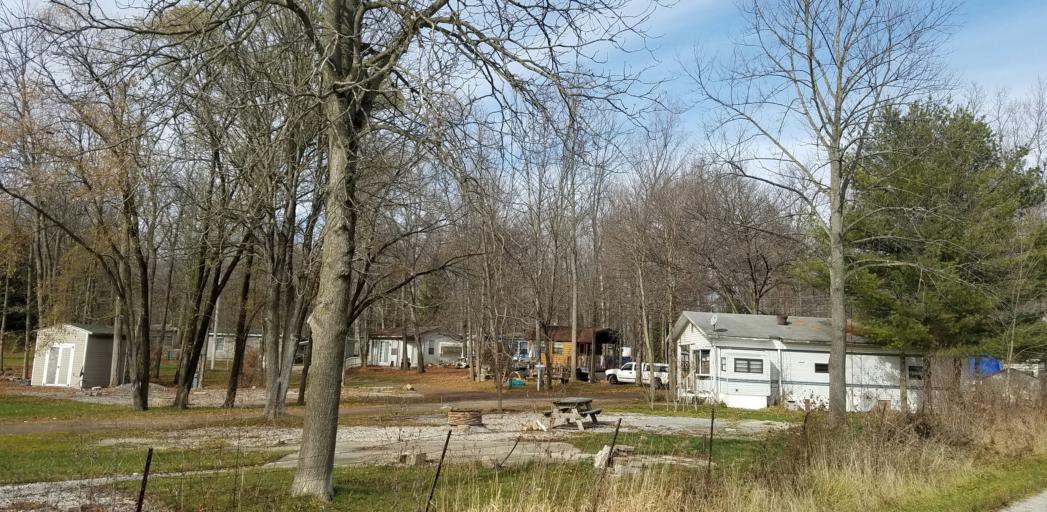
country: US
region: Ohio
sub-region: Morrow County
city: Mount Gilead
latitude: 40.5492
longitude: -82.7584
